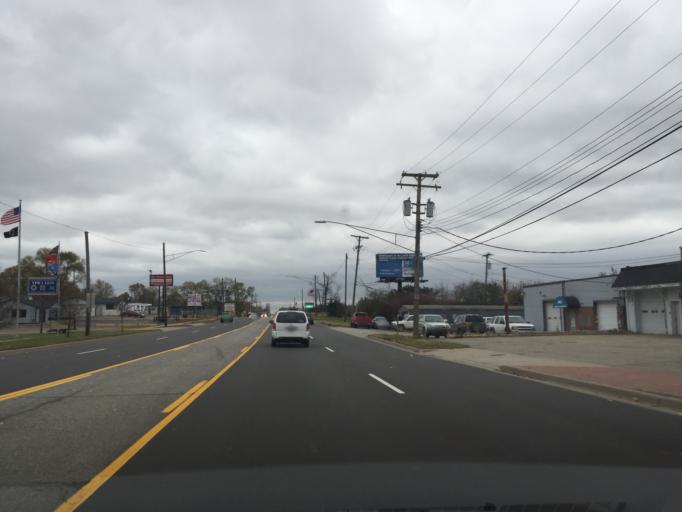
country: US
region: Michigan
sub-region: Oakland County
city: Pontiac
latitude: 42.6562
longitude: -83.3155
